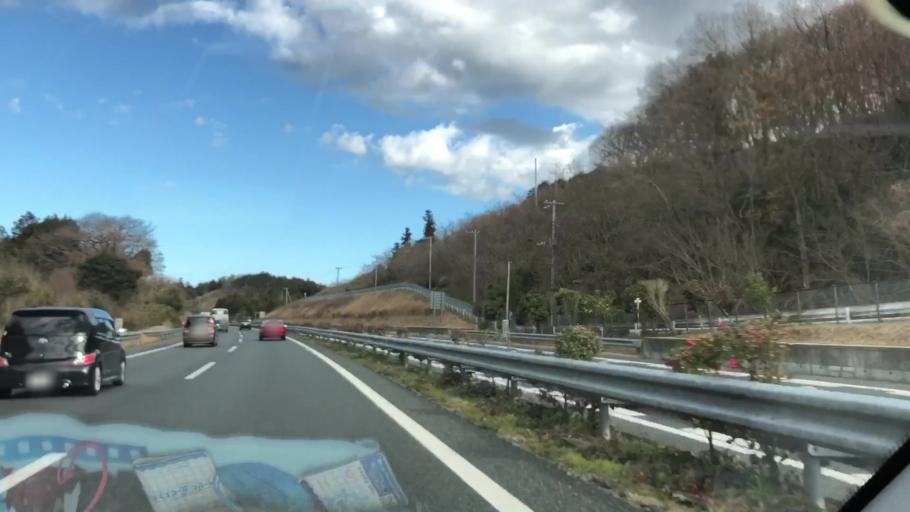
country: JP
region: Chiba
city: Kisarazu
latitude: 35.3268
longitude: 139.9463
